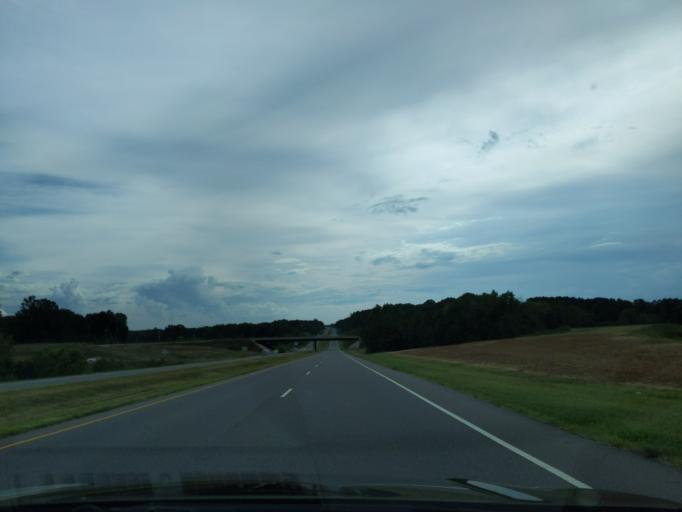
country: US
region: North Carolina
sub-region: Cabarrus County
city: Mount Pleasant
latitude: 35.4082
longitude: -80.4488
